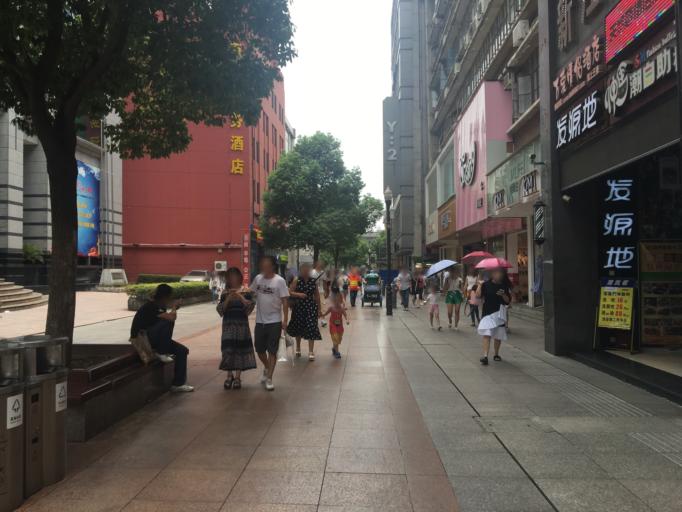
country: CN
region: Hubei
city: Wuhan
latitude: 30.5802
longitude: 114.2900
